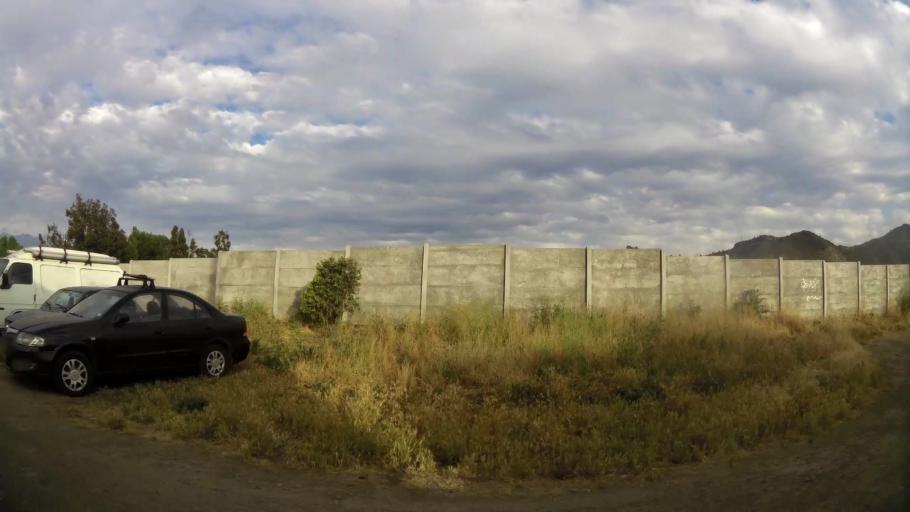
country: CL
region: Santiago Metropolitan
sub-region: Provincia de Maipo
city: San Bernardo
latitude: -33.6480
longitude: -70.6607
